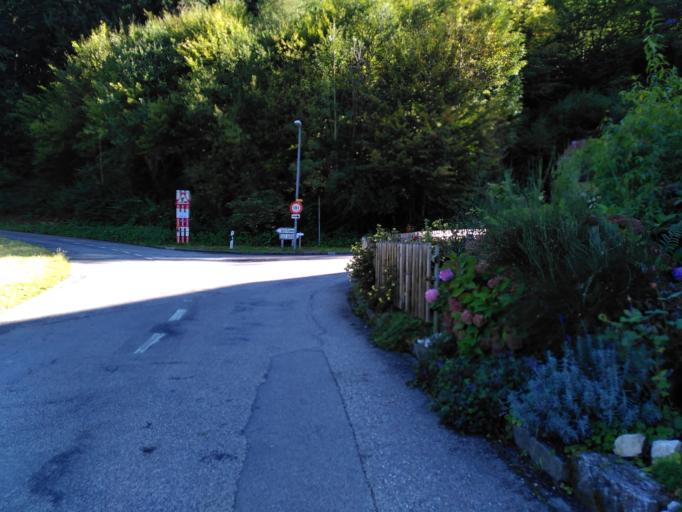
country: CH
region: Bern
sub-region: Oberaargau
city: Seeberg
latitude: 47.1393
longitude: 7.7023
